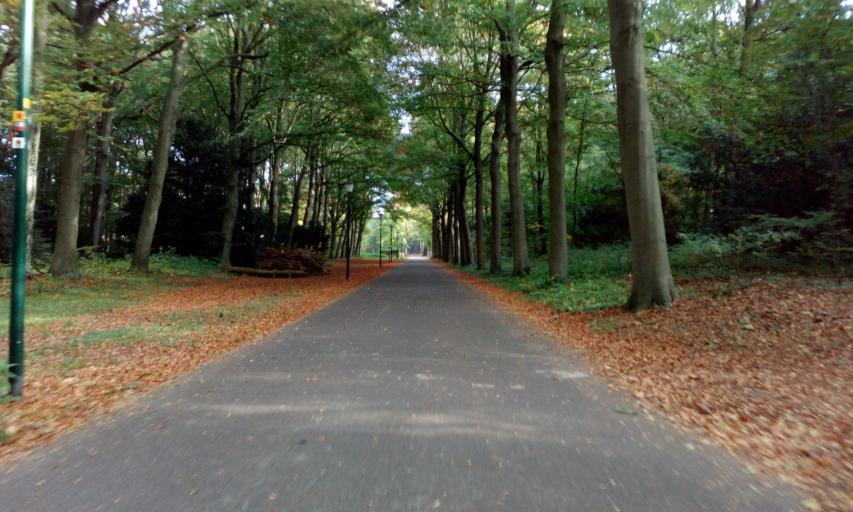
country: NL
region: South Holland
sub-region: Gemeente Wassenaar
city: Wassenaar
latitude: 52.1199
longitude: 4.3757
